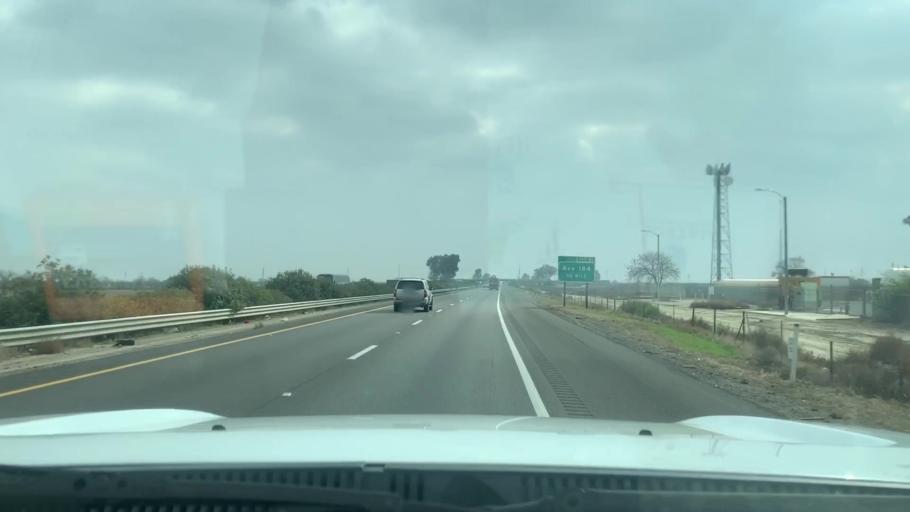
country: US
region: California
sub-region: Tulare County
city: Tipton
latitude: 36.1311
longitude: -119.3256
